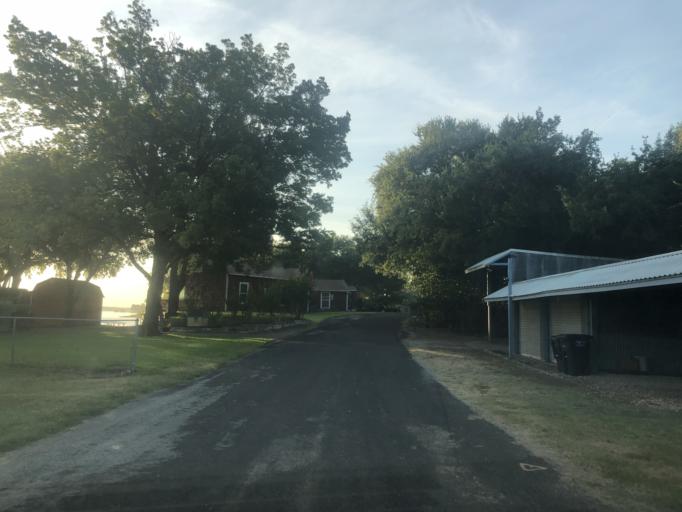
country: US
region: Texas
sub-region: Tarrant County
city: Lakeside
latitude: 32.7988
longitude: -97.4902
